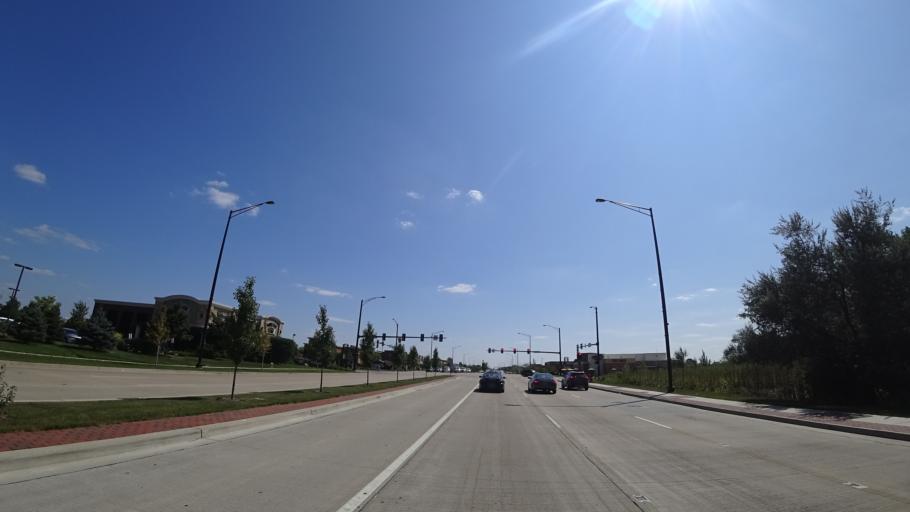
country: US
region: Illinois
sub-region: Cook County
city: Orland Park
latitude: 41.6079
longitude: -87.8532
